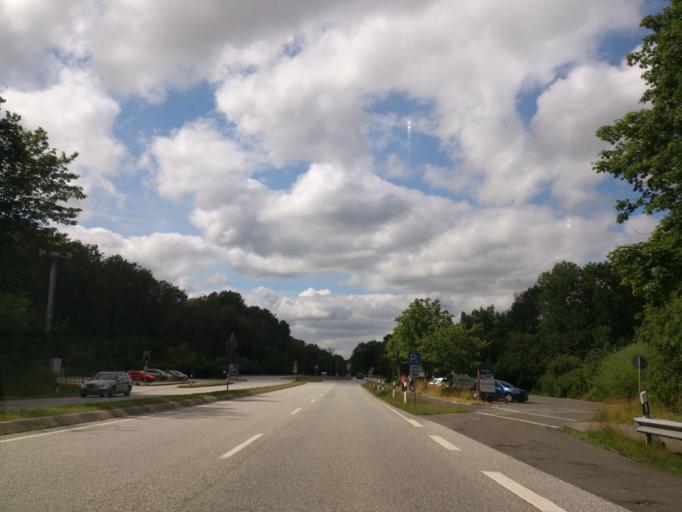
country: DK
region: South Denmark
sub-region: Aabenraa Kommune
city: Krusa
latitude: 54.8374
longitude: 9.4085
